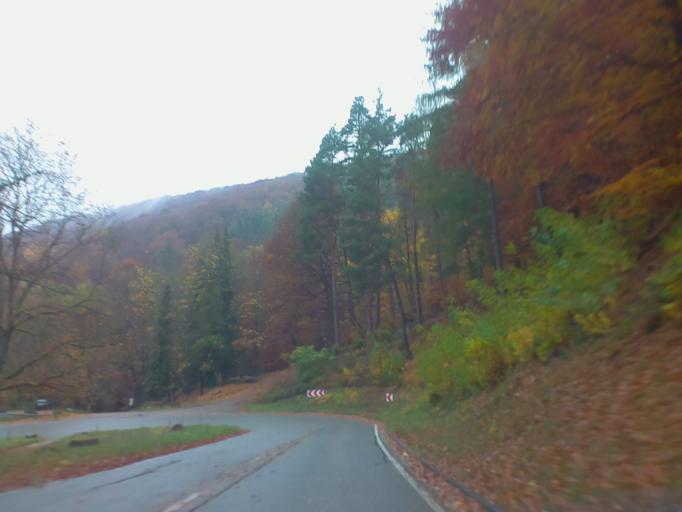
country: DE
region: Hesse
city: Neckarsteinach
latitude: 49.4094
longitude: 8.8432
